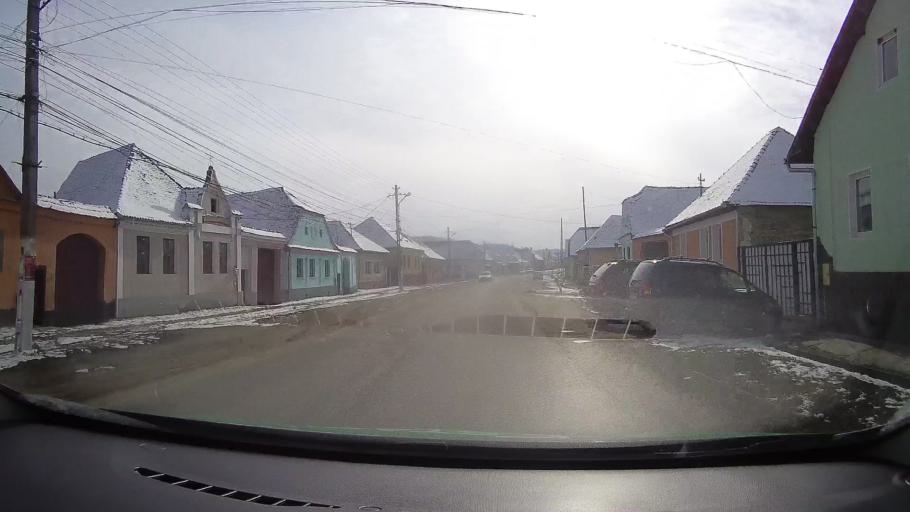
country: RO
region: Sibiu
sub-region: Comuna Laslea
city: Laslea
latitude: 46.2089
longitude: 24.6565
